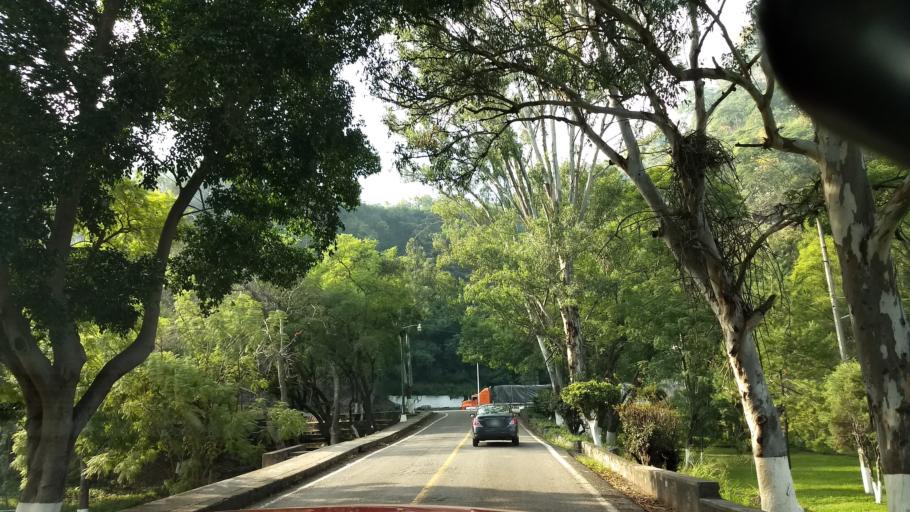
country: MX
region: Jalisco
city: Tuxpan
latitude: 19.5289
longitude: -103.4400
